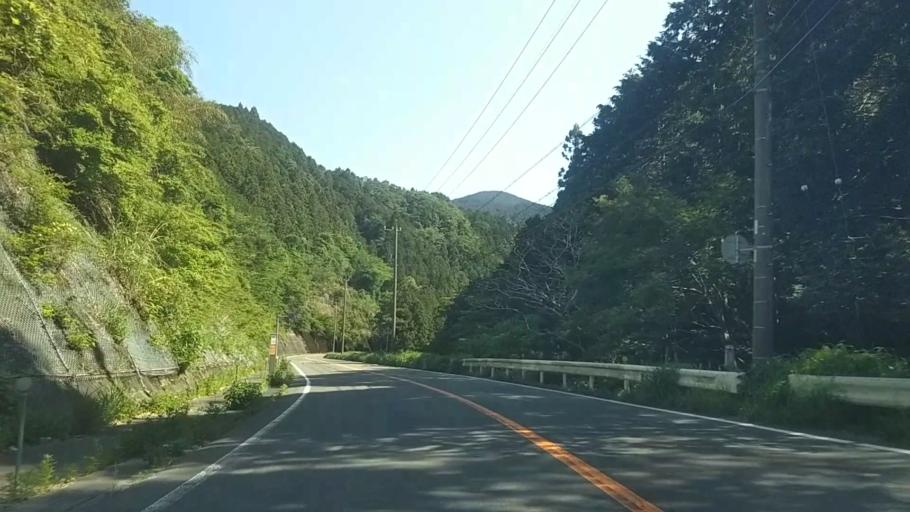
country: JP
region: Shizuoka
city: Fujinomiya
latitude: 35.1898
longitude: 138.5298
